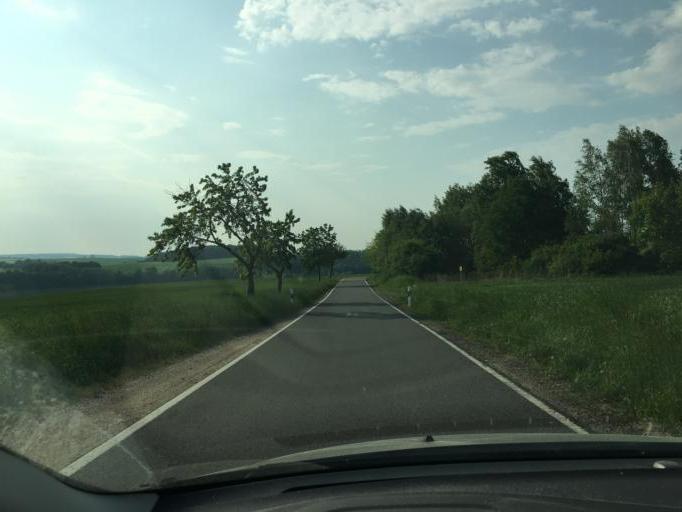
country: DE
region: Saxony
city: Rochlitz
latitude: 51.0646
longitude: 12.7999
